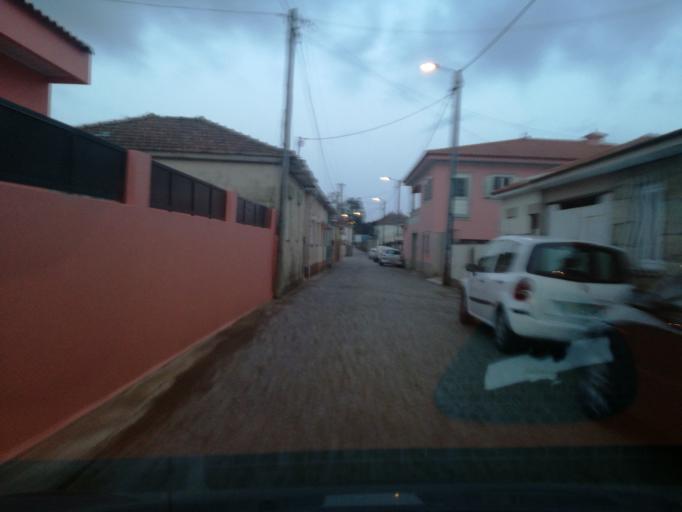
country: PT
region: Porto
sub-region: Maia
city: Gemunde
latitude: 41.2684
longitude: -8.6567
